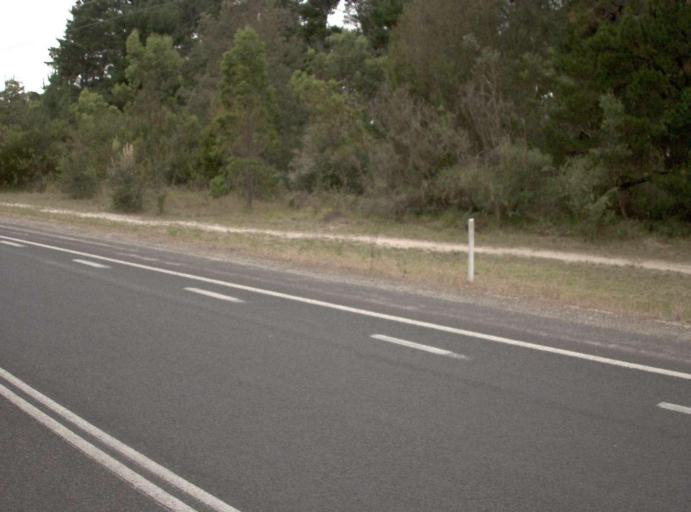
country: AU
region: Victoria
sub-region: Wellington
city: Sale
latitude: -38.1728
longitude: 147.0882
